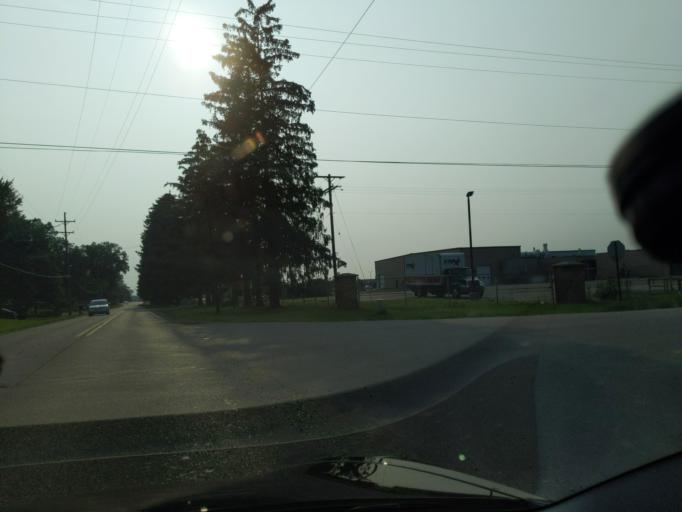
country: US
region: Michigan
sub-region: Jackson County
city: Jackson
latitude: 42.2620
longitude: -84.4428
